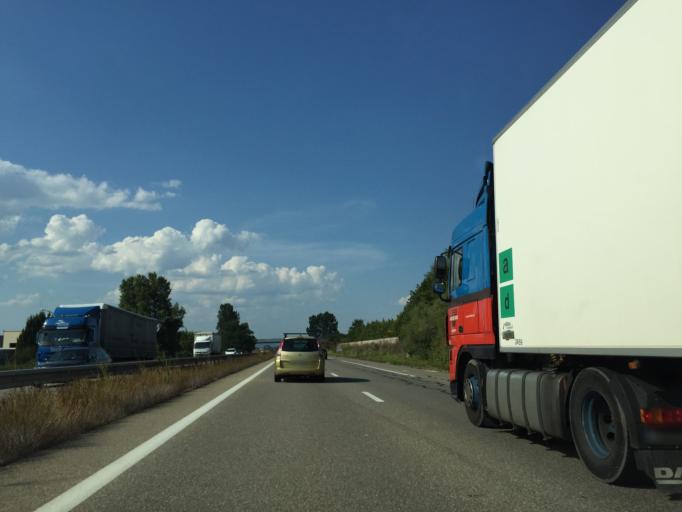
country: FR
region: Alsace
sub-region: Departement du Haut-Rhin
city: Houssen
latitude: 48.1045
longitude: 7.3827
